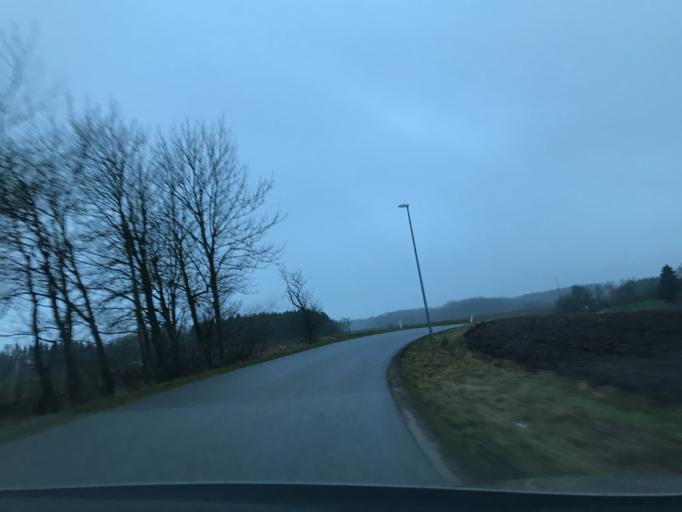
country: DK
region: South Denmark
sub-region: Vejle Kommune
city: Brejning
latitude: 55.6920
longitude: 9.7701
